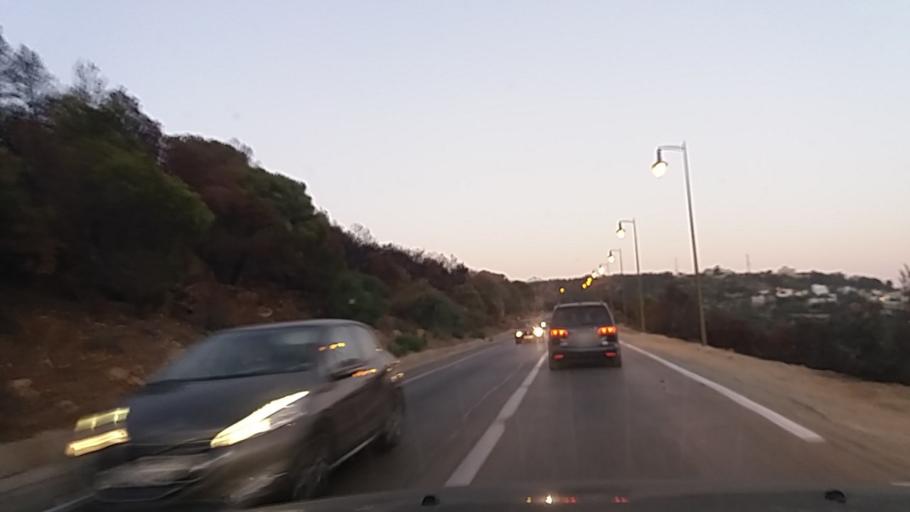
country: MA
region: Tanger-Tetouan
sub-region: Tanger-Assilah
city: Boukhalef
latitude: 35.7778
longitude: -5.9215
